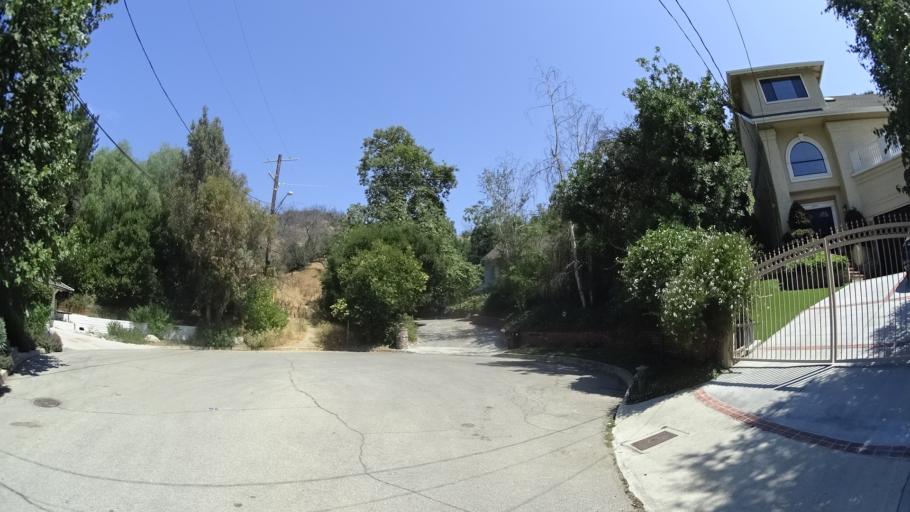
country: US
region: California
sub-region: Los Angeles County
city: North Hollywood
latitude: 34.1367
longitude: -118.4055
